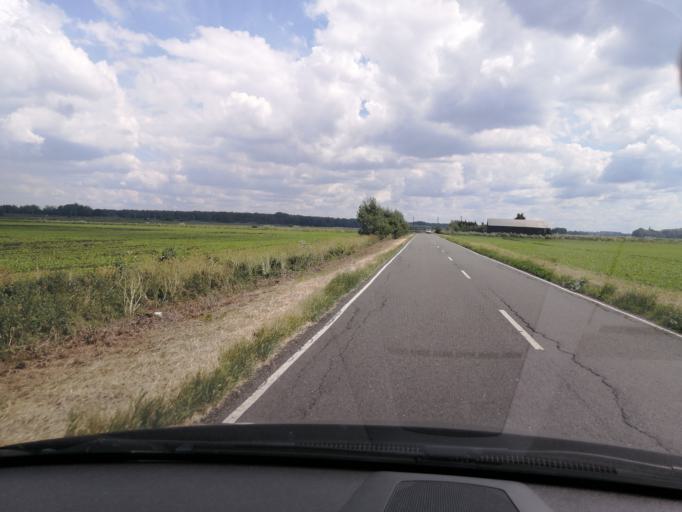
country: GB
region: England
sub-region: Cambridgeshire
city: Yaxley
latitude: 52.5002
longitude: -0.2499
